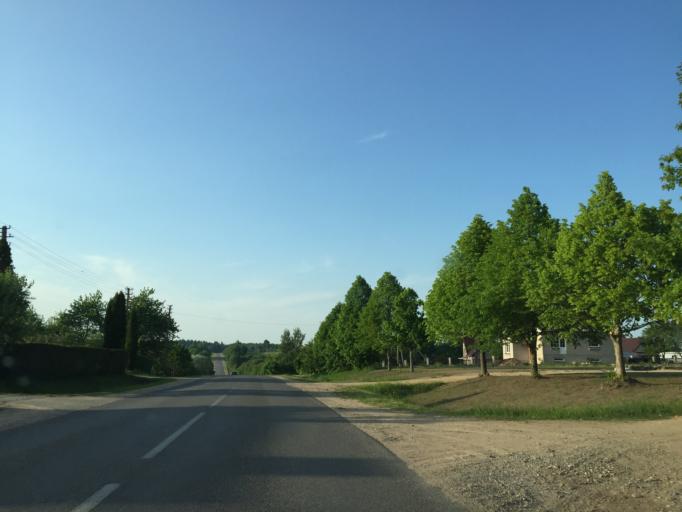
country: LT
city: Plateliai
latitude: 56.0492
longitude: 21.8188
